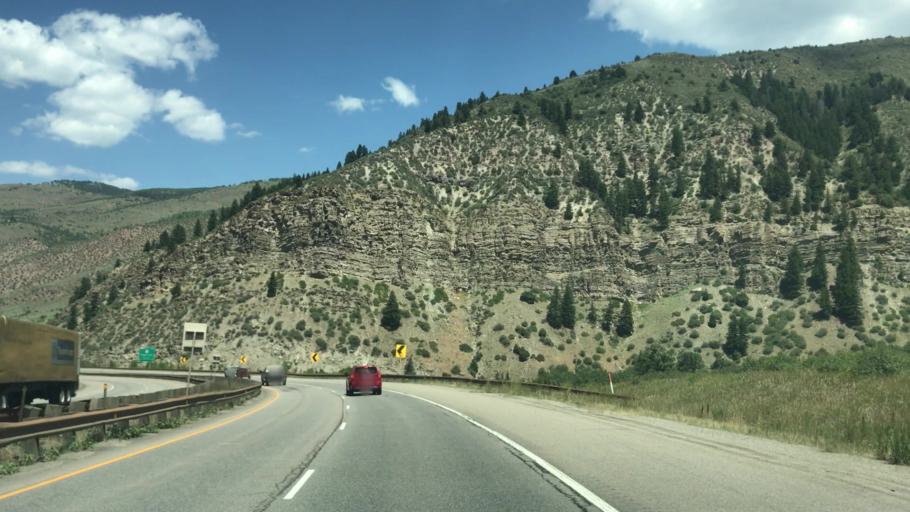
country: US
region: Colorado
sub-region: Eagle County
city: Minturn
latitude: 39.6146
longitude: -106.4590
